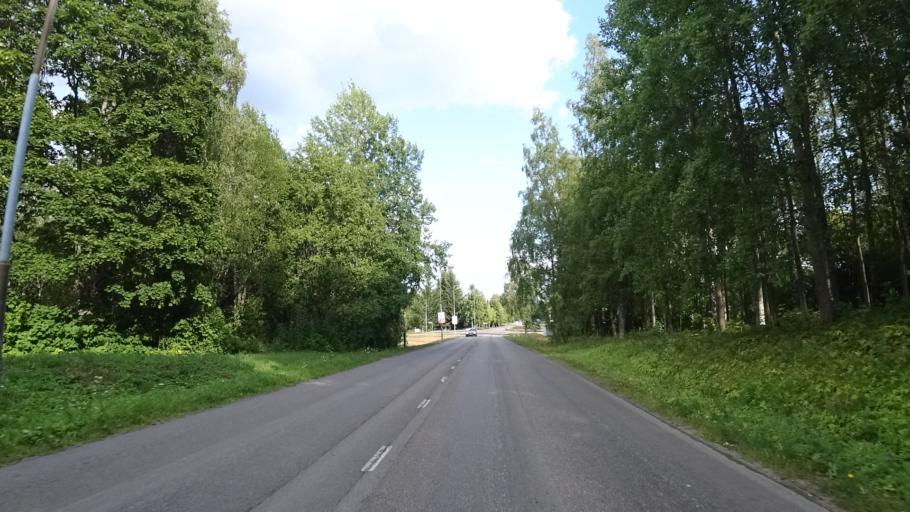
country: FI
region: South Karelia
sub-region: Imatra
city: Imatra
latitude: 61.1710
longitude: 28.7566
